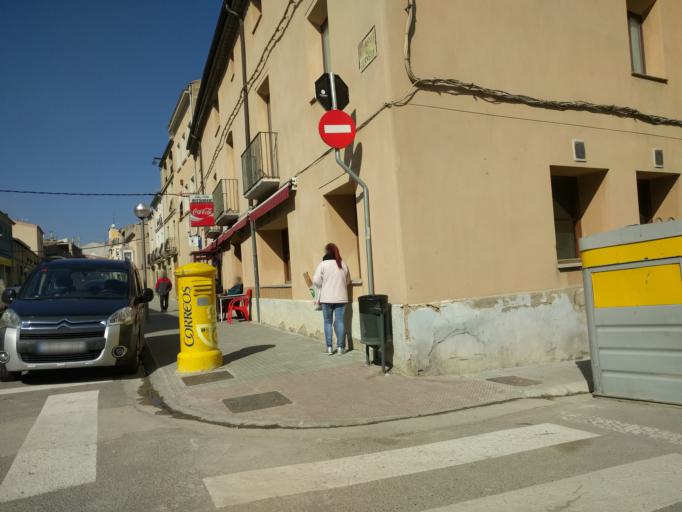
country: ES
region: Catalonia
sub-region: Provincia de Tarragona
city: Santa Coloma de Queralt
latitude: 41.5331
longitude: 1.3831
